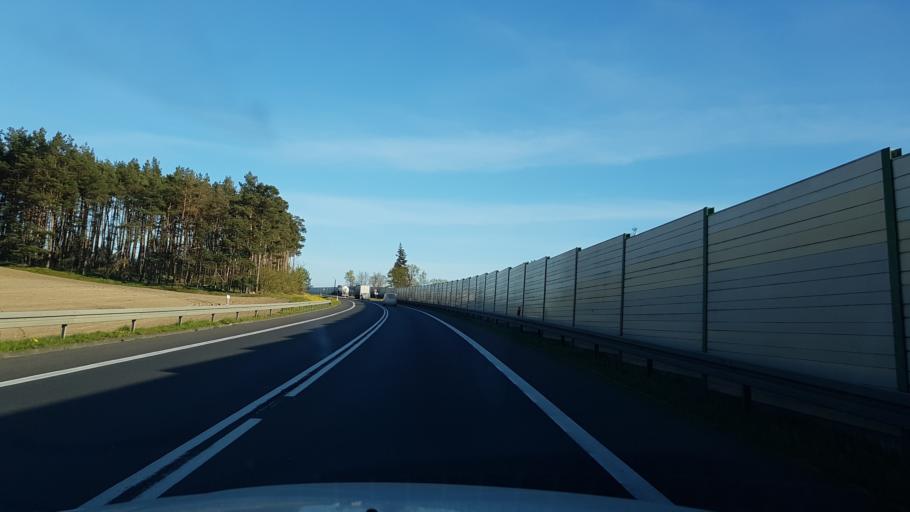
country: PL
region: West Pomeranian Voivodeship
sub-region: Powiat kamienski
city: Wolin
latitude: 53.8706
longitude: 14.5410
